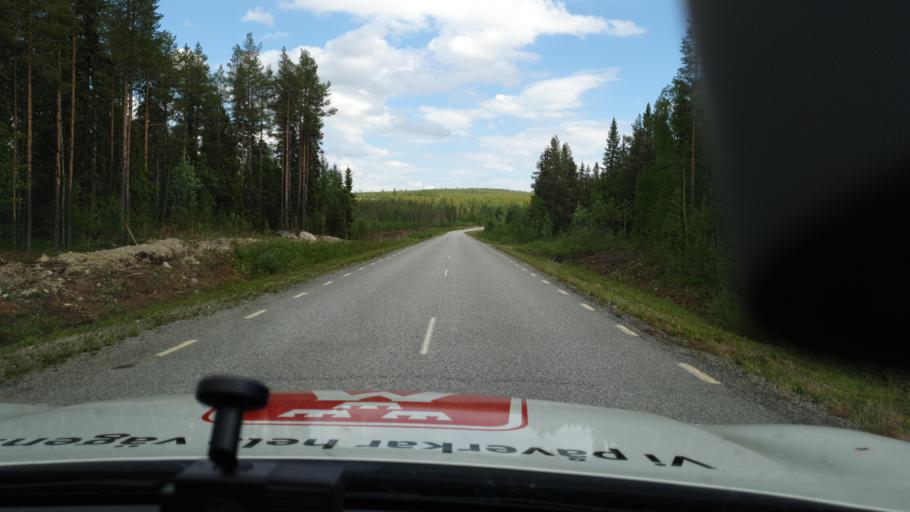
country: SE
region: Vaesterbotten
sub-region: Sorsele Kommun
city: Sorsele
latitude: 65.1749
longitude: 17.5922
